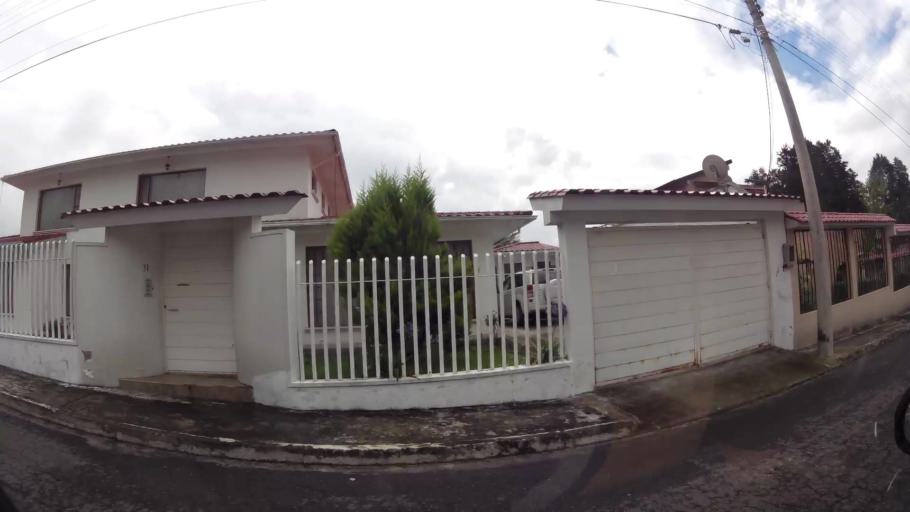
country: EC
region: Pichincha
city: Sangolqui
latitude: -0.3058
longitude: -78.4805
